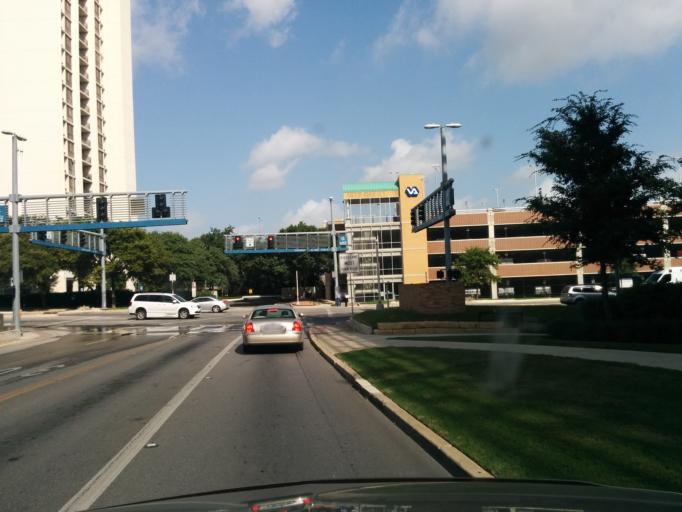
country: US
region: Texas
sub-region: Bexar County
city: Balcones Heights
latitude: 29.5084
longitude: -98.5805
